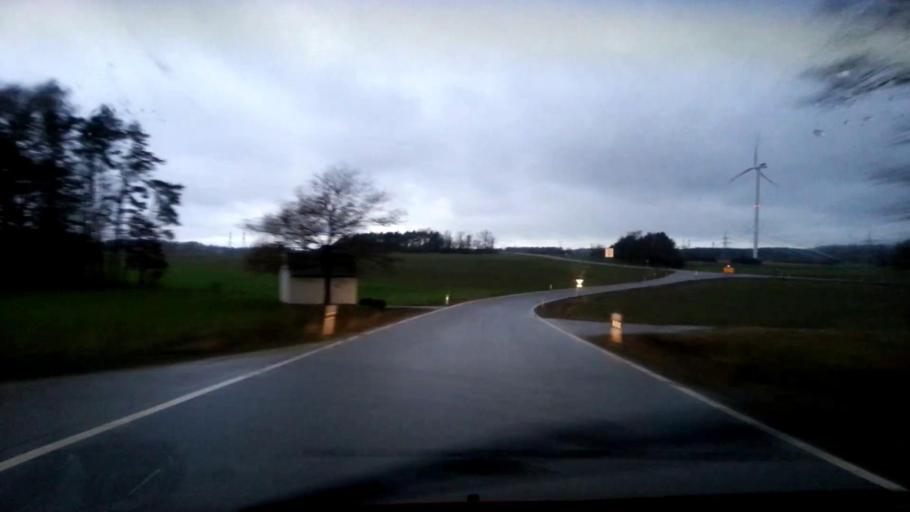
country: DE
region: Bavaria
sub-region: Upper Franconia
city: Poxdorf
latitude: 49.9727
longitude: 11.1216
